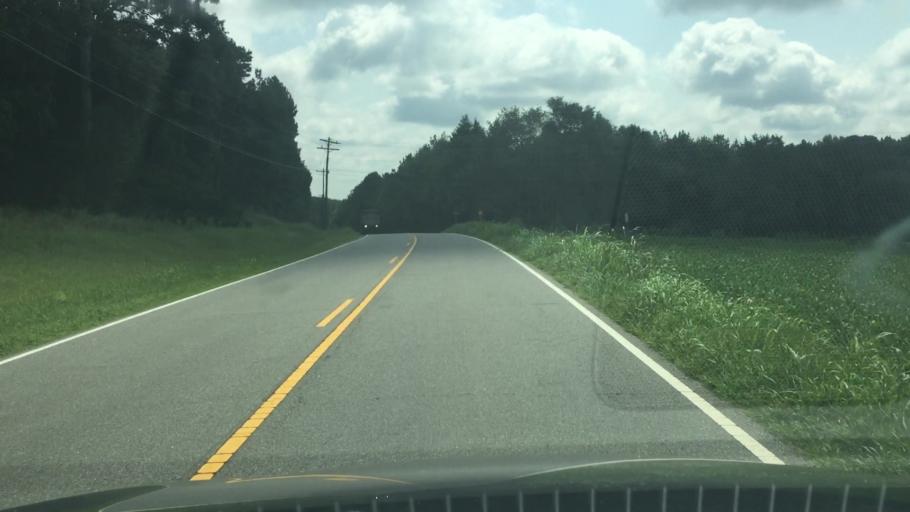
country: US
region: North Carolina
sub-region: Gaston County
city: Davidson
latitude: 35.4875
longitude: -80.7570
